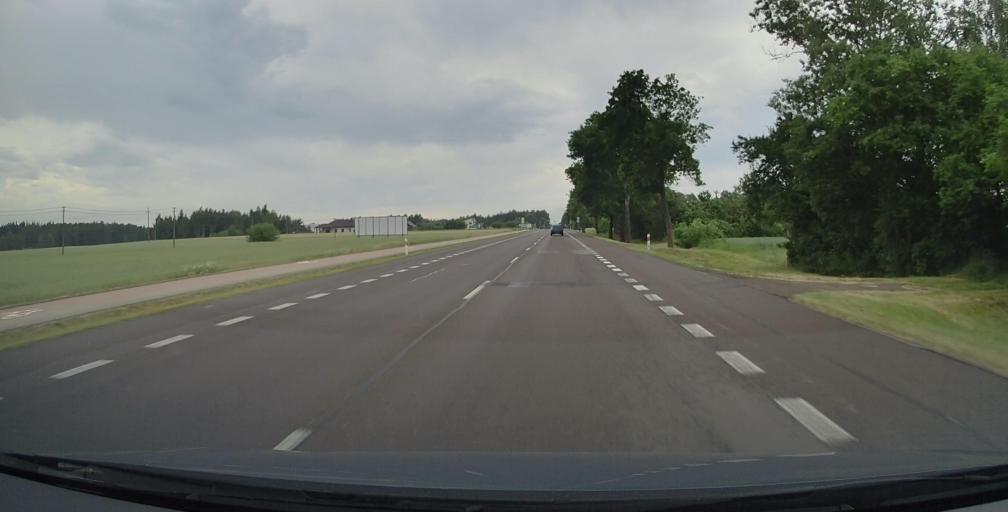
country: PL
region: Lublin Voivodeship
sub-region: Powiat bialski
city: Lesna Podlaska
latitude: 52.0359
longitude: 23.0111
